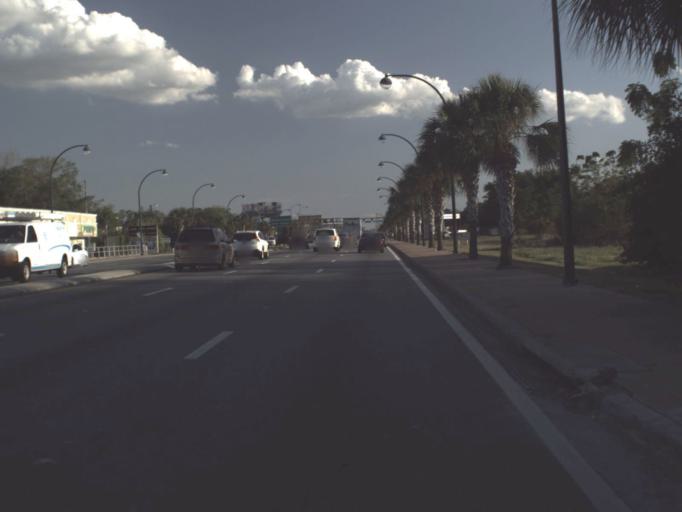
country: US
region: Florida
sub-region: Orange County
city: Holden Heights
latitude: 28.4871
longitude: -81.3969
